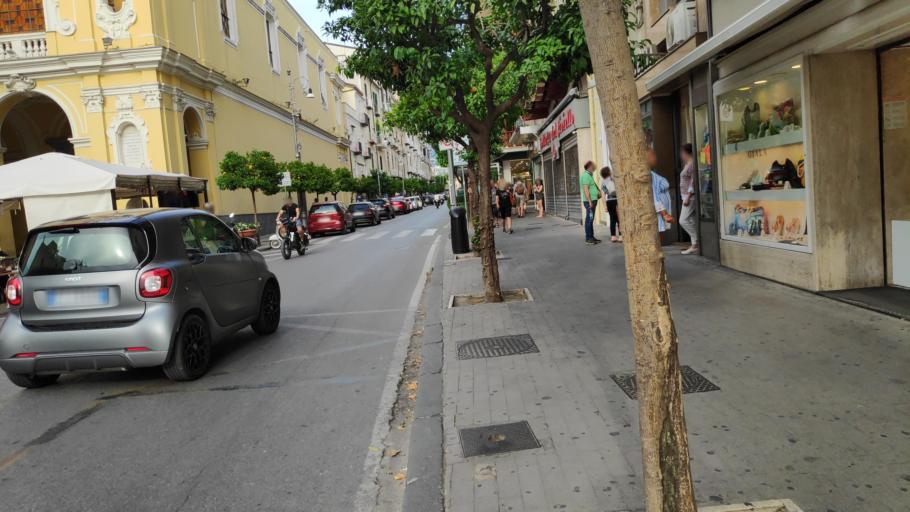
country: IT
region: Campania
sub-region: Provincia di Napoli
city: Sorrento
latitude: 40.6261
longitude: 14.3759
